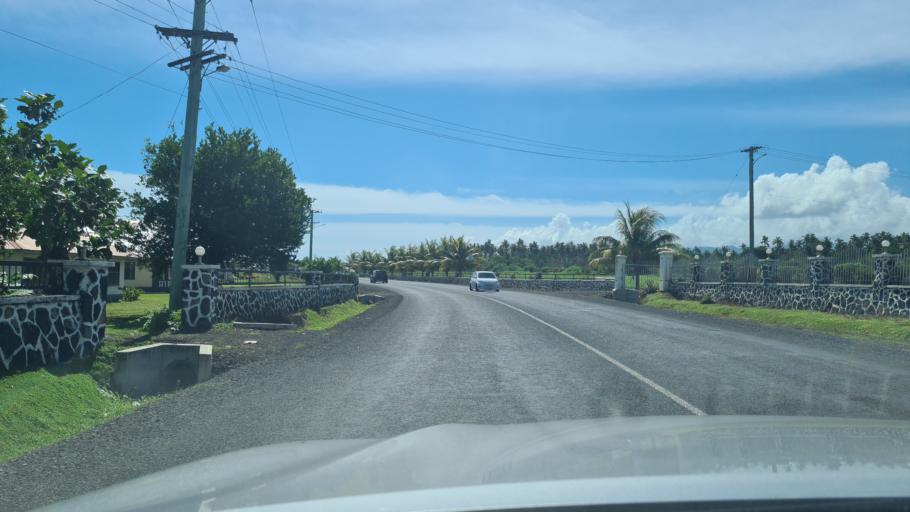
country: WS
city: Faleula
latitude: -13.7997
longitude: -171.8269
